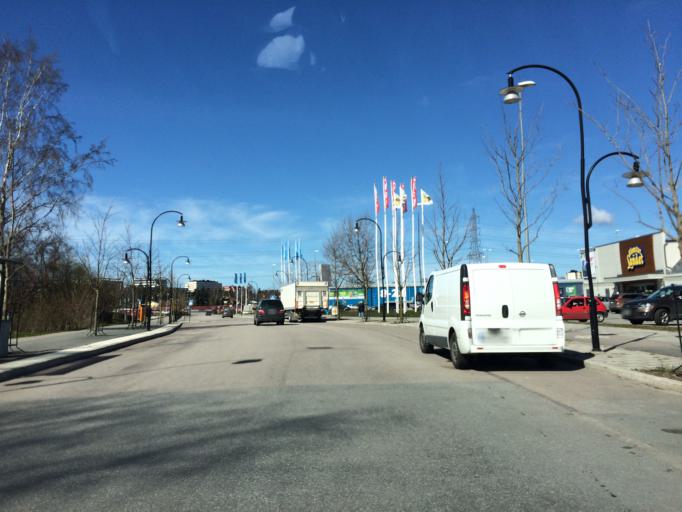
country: SE
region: Stockholm
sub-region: Sollentuna Kommun
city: Sollentuna
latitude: 59.4387
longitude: 17.9348
